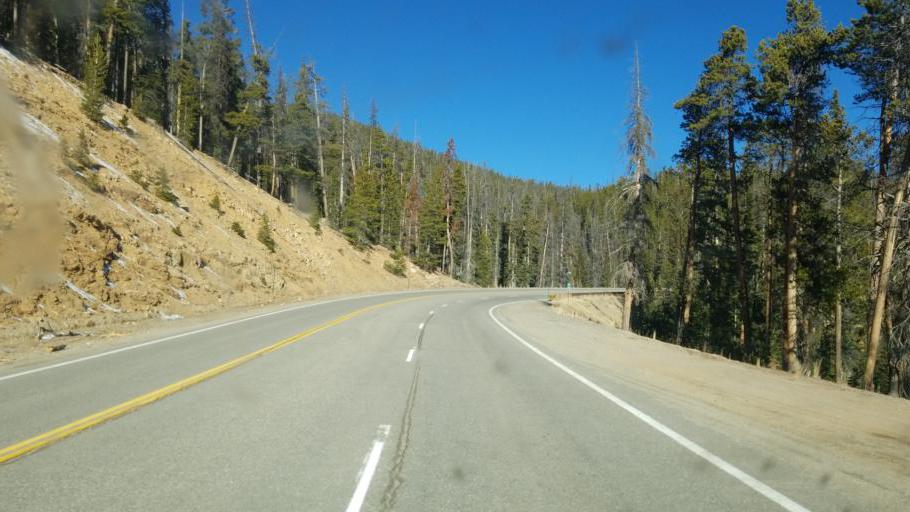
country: US
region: Colorado
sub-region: Chaffee County
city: Salida
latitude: 38.4752
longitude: -106.3355
